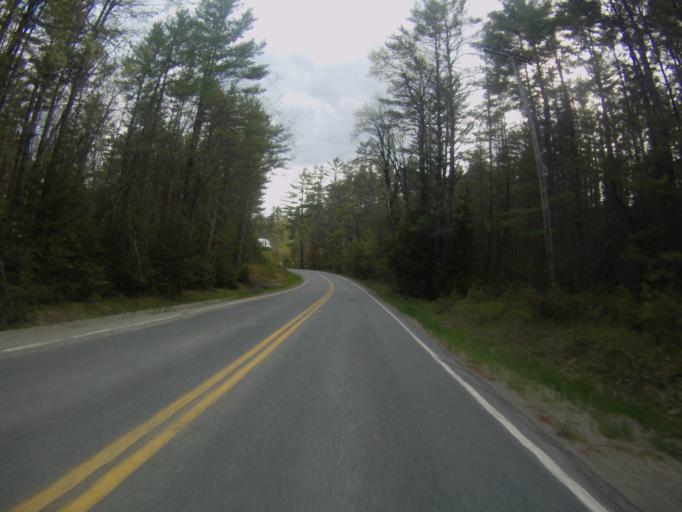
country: US
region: New York
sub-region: Warren County
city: Warrensburg
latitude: 43.8350
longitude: -73.8957
